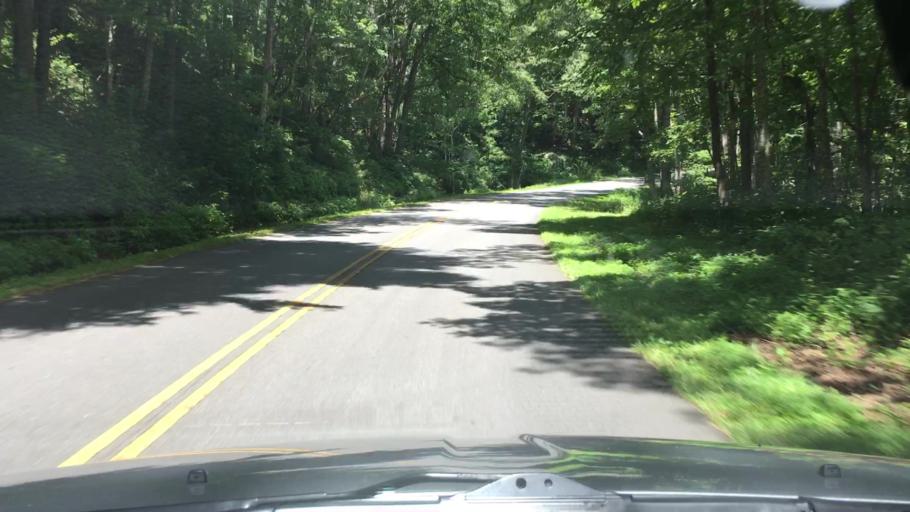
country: US
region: North Carolina
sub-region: Buncombe County
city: Swannanoa
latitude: 35.6671
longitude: -82.4478
